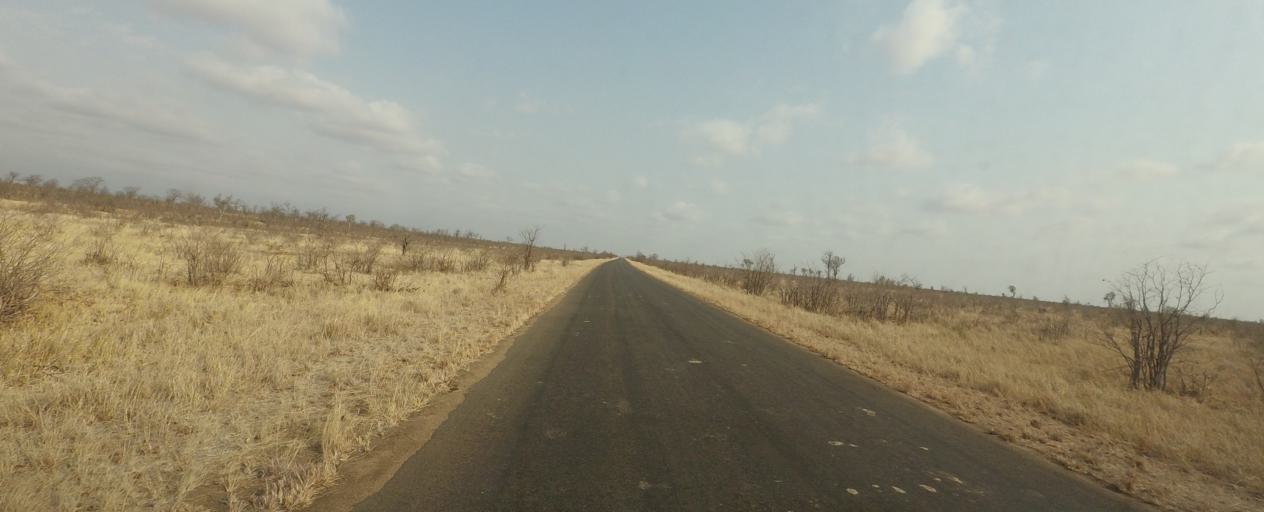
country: ZA
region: Limpopo
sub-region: Vhembe District Municipality
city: Mutale
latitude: -22.9273
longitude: 31.2607
